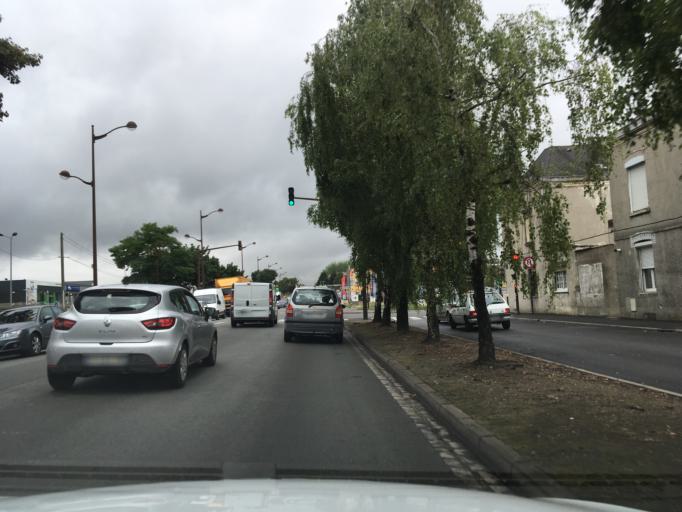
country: FR
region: Picardie
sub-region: Departement de l'Aisne
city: Saint-Quentin
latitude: 49.8479
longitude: 3.2722
